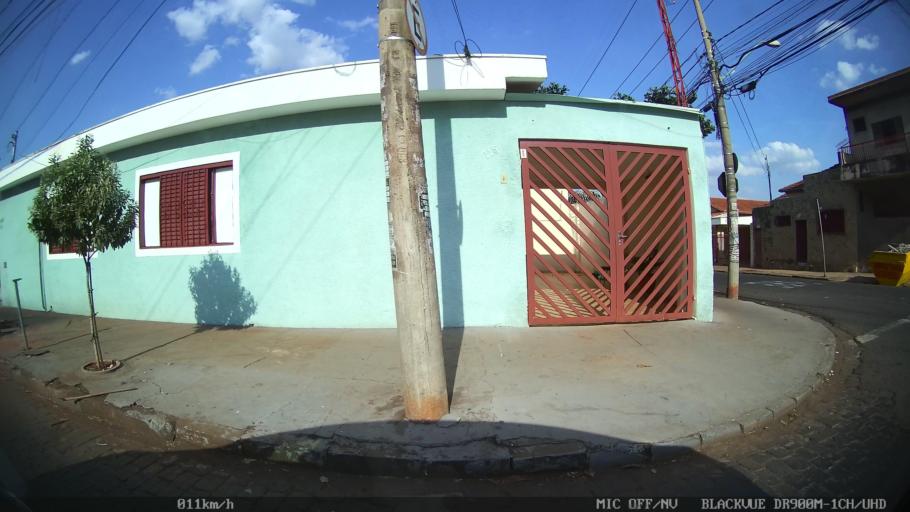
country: BR
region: Sao Paulo
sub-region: Ribeirao Preto
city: Ribeirao Preto
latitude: -21.1718
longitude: -47.8187
